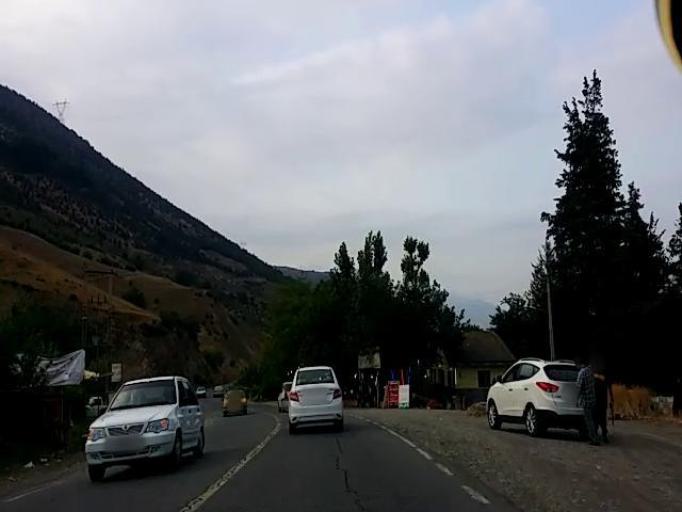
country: IR
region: Mazandaran
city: Chalus
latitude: 36.4113
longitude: 51.2789
